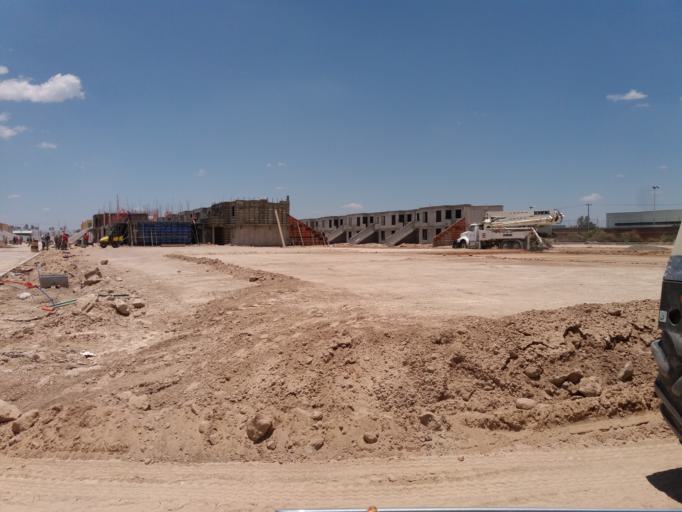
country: MX
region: Aguascalientes
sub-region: Aguascalientes
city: San Sebastian [Fraccionamiento]
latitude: 21.8089
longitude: -102.2757
